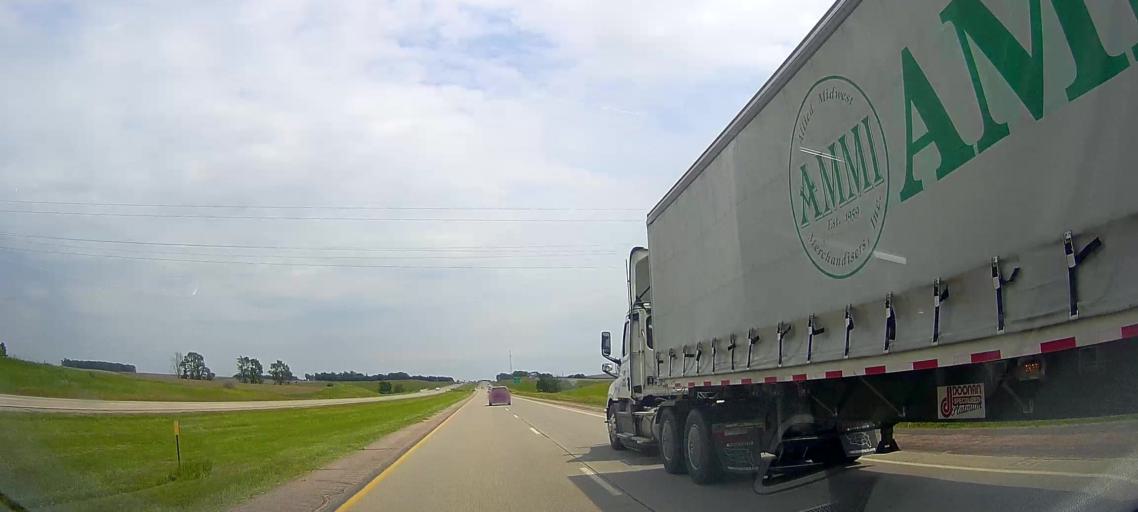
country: US
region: South Dakota
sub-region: Minnehaha County
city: Crooks
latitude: 43.6087
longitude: -96.8308
